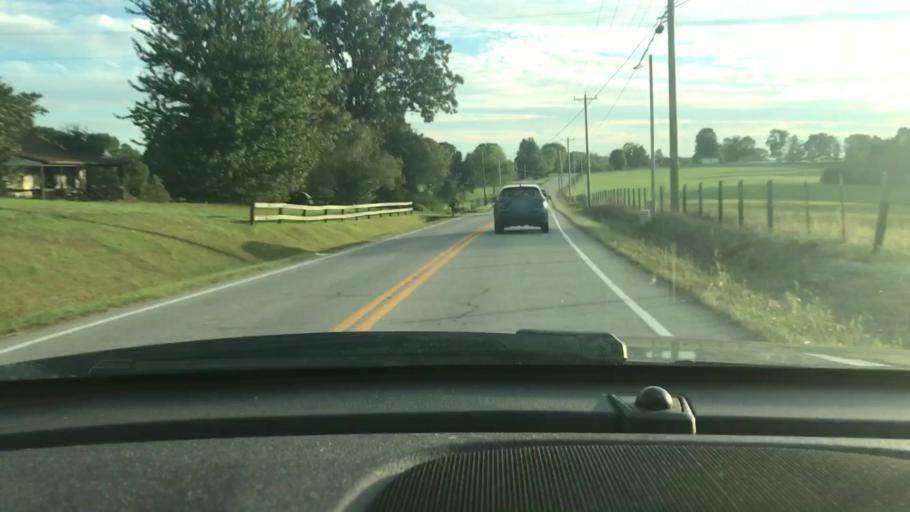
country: US
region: Tennessee
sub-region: Dickson County
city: Charlotte
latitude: 36.2386
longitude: -87.2460
